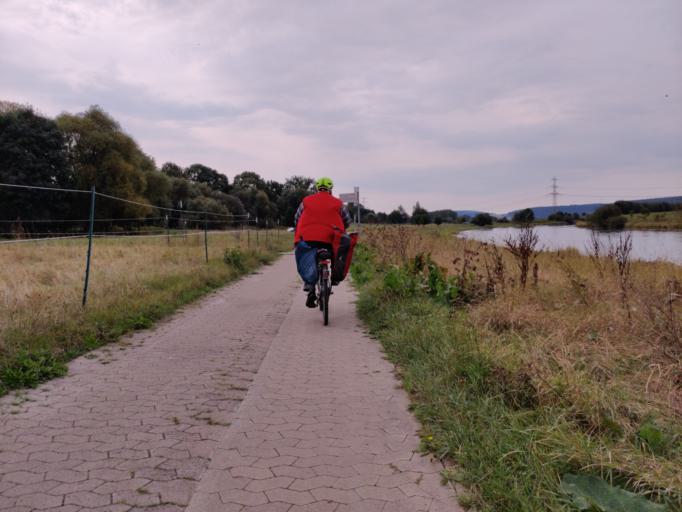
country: DE
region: Lower Saxony
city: Hehlen
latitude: 52.0316
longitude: 9.4280
